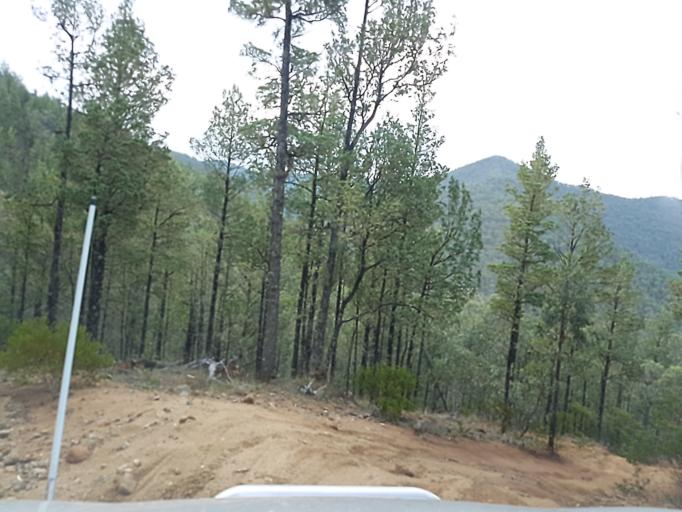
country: AU
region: New South Wales
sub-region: Snowy River
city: Jindabyne
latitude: -36.9522
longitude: 148.3798
